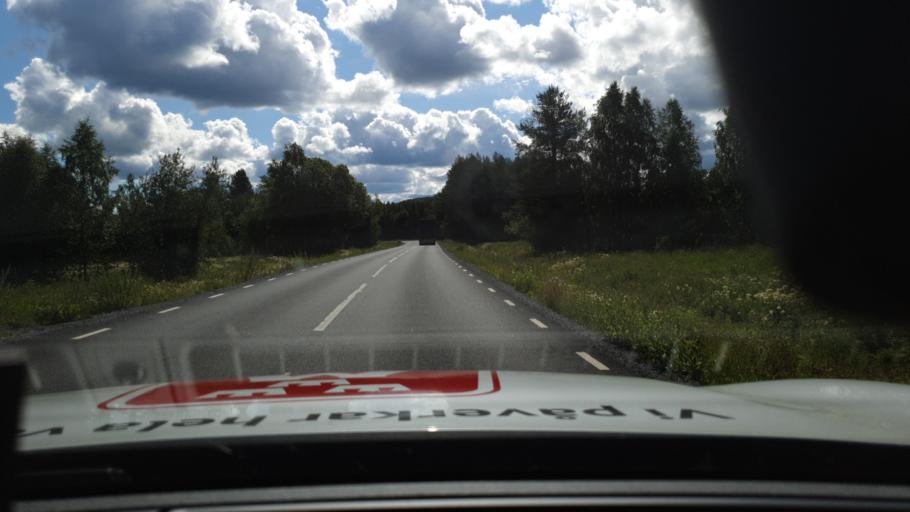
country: SE
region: Norrbotten
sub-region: Bodens Kommun
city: Boden
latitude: 65.8453
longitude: 21.7391
